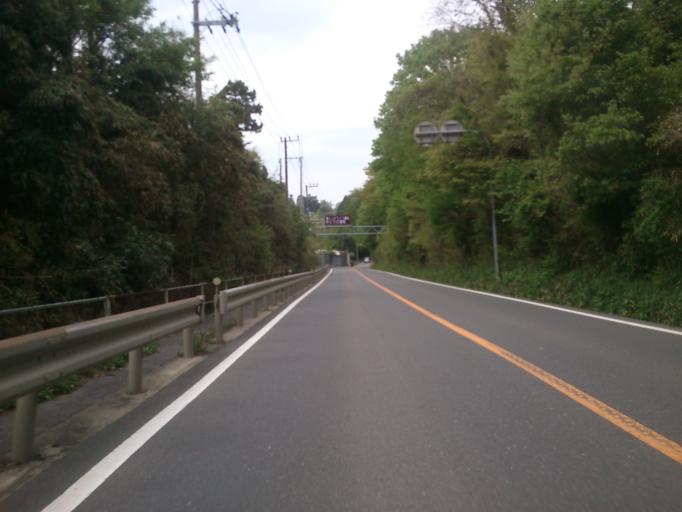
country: JP
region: Kyoto
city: Kameoka
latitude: 34.9476
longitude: 135.4971
